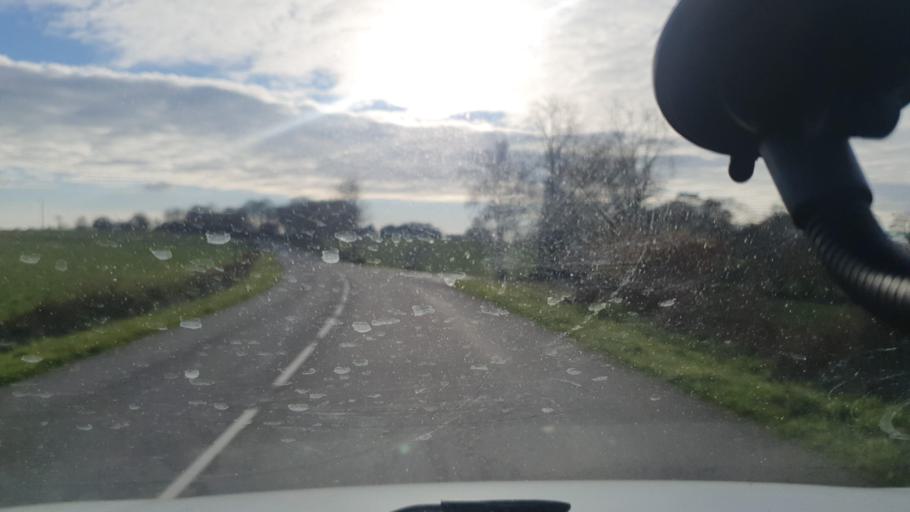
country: FR
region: Brittany
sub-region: Departement du Finistere
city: Briec
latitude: 48.0718
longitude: -4.0192
